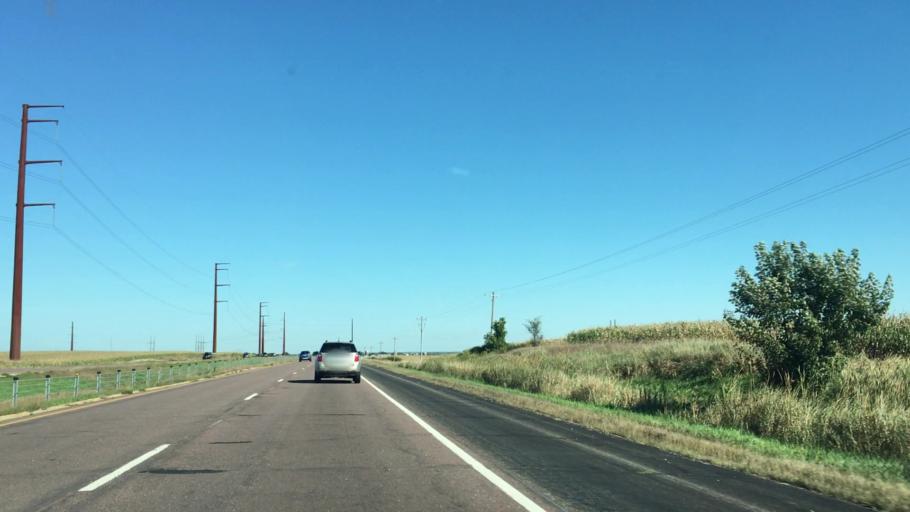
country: US
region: Minnesota
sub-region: Dakota County
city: Farmington
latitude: 44.6292
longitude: -92.9943
